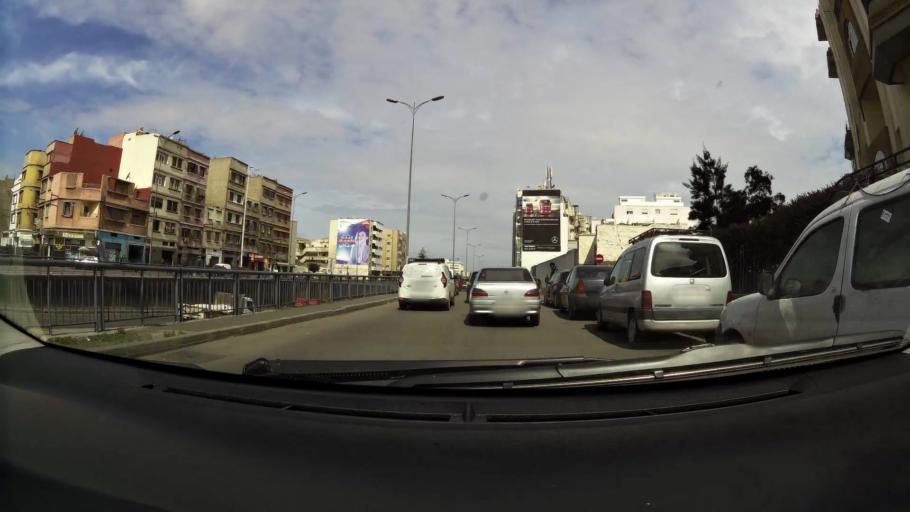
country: MA
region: Grand Casablanca
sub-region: Casablanca
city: Casablanca
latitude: 33.5775
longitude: -7.5875
